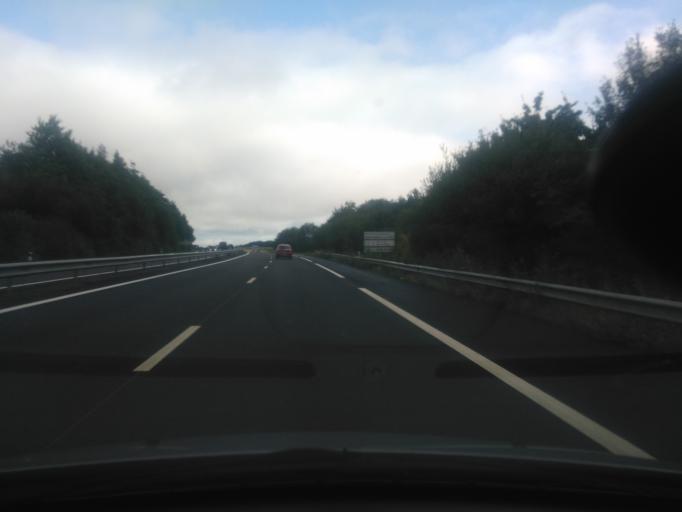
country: FR
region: Brittany
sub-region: Departement d'Ille-et-Vilaine
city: Hede-Bazouges
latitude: 48.2887
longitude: -1.8035
